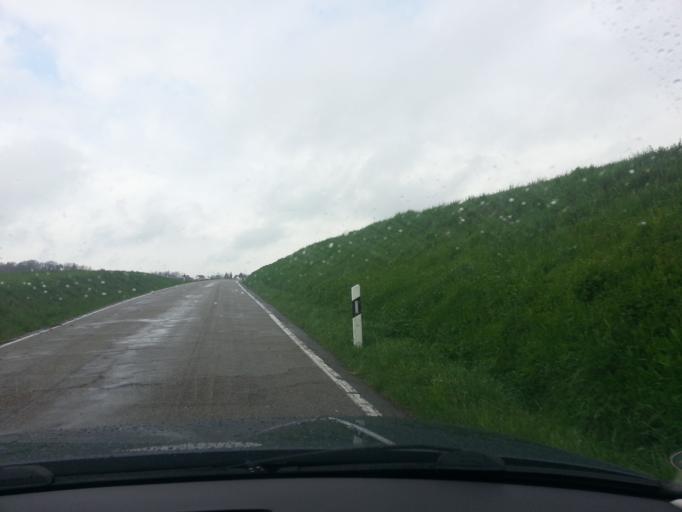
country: DE
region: Rheinland-Pfalz
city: Massweiler
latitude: 49.2600
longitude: 7.5415
